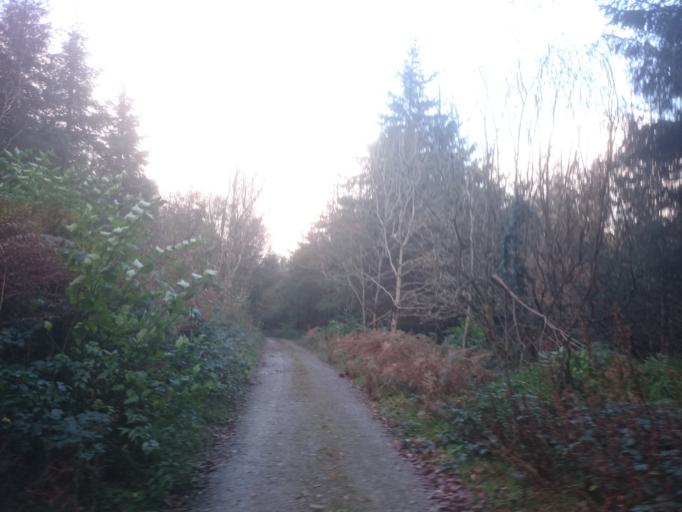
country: IE
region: Leinster
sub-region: Kilkenny
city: Thomastown
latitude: 52.4672
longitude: -7.0560
